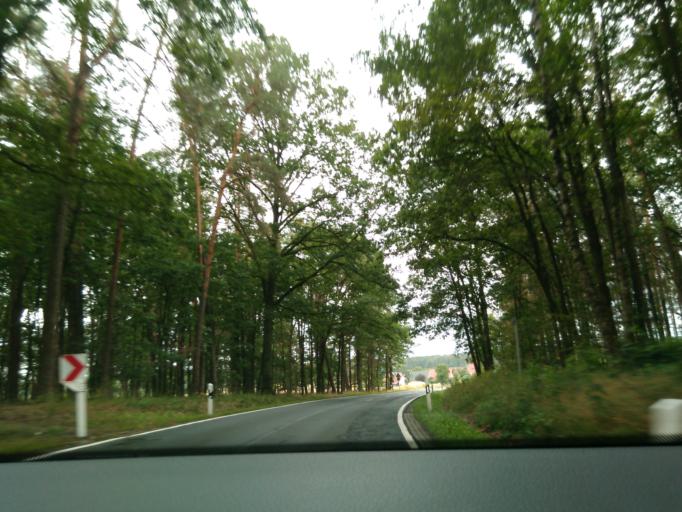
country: DE
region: Bavaria
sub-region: Regierungsbezirk Mittelfranken
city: Gremsdorf
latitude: 49.6618
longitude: 10.8080
